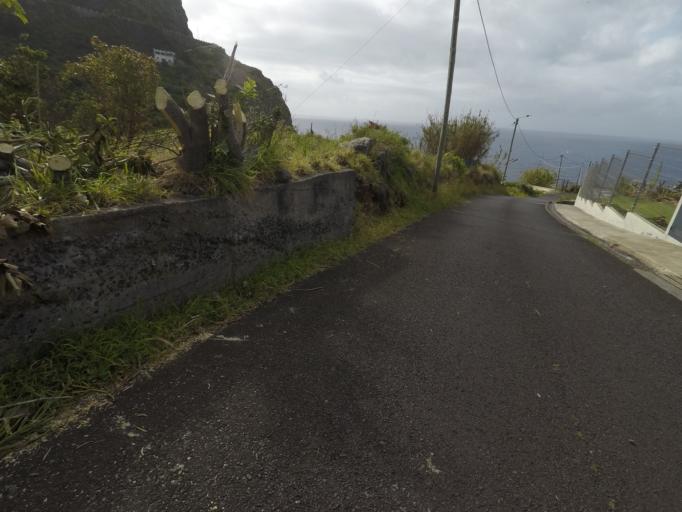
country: PT
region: Madeira
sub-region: Sao Vicente
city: Sao Vicente
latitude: 32.8269
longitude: -16.9743
